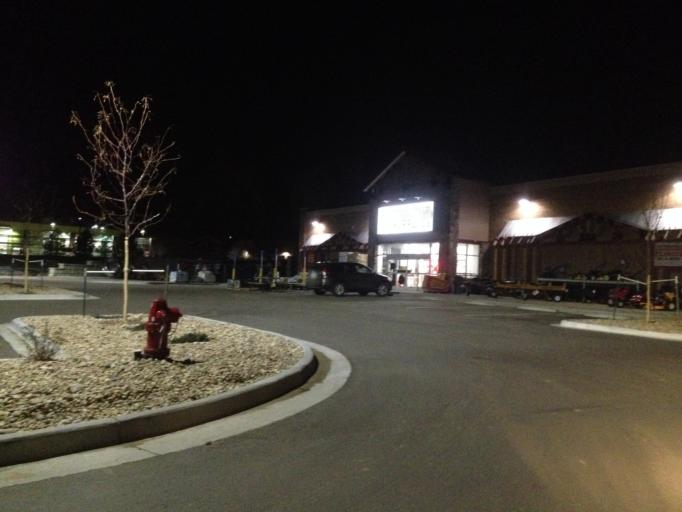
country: US
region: Colorado
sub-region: Boulder County
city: Lafayette
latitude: 40.0084
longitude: -105.1047
